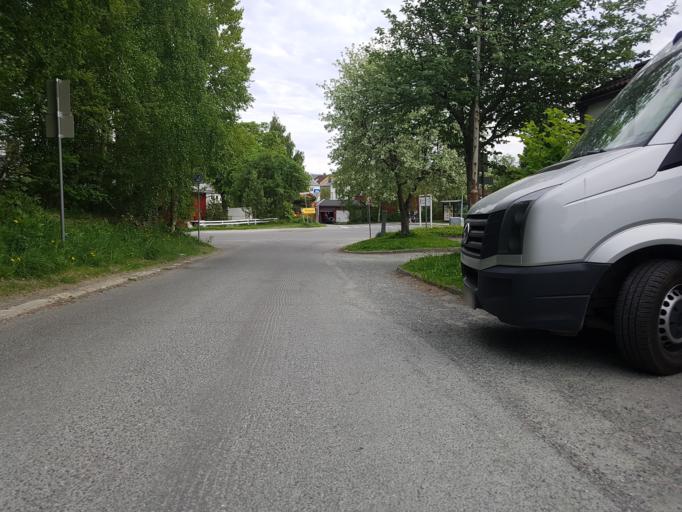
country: NO
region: Sor-Trondelag
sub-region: Trondheim
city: Trondheim
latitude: 63.4281
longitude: 10.4323
